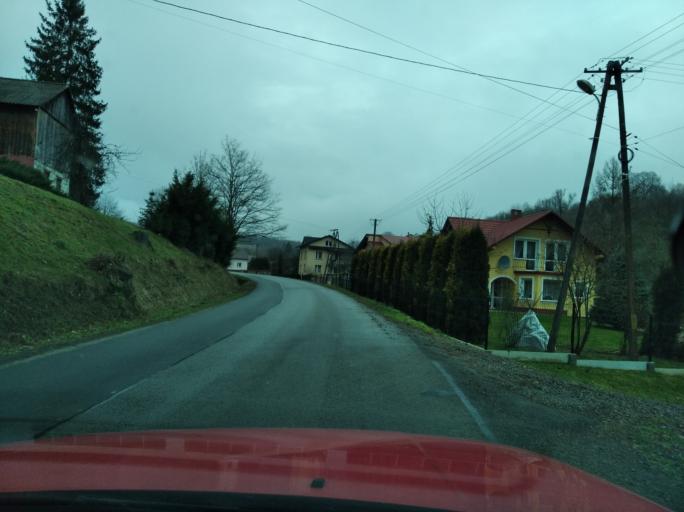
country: PL
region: Subcarpathian Voivodeship
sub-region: Powiat przemyski
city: Nienadowa
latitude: 49.8493
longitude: 22.4288
